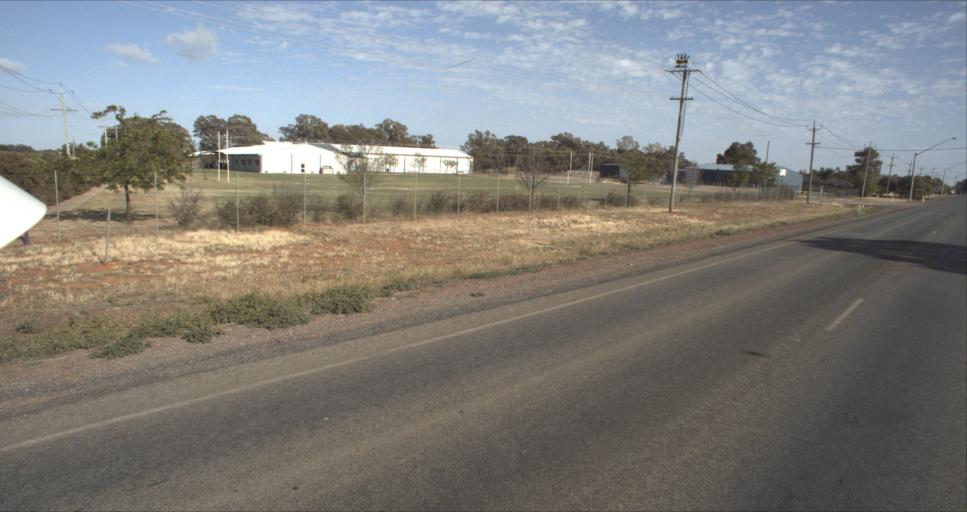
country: AU
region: New South Wales
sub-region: Leeton
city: Leeton
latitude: -34.5648
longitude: 146.3932
